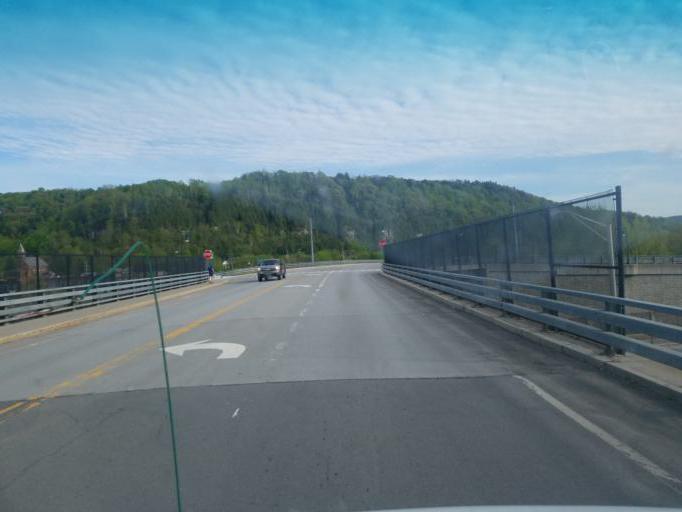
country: US
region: New York
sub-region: Herkimer County
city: Little Falls
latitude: 43.0418
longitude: -74.8610
